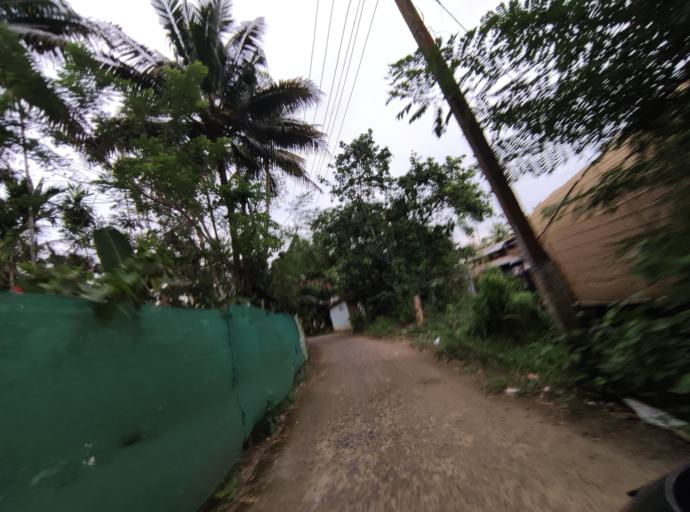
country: IN
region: Kerala
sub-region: Alappuzha
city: Shertallai
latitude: 9.6298
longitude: 76.4281
